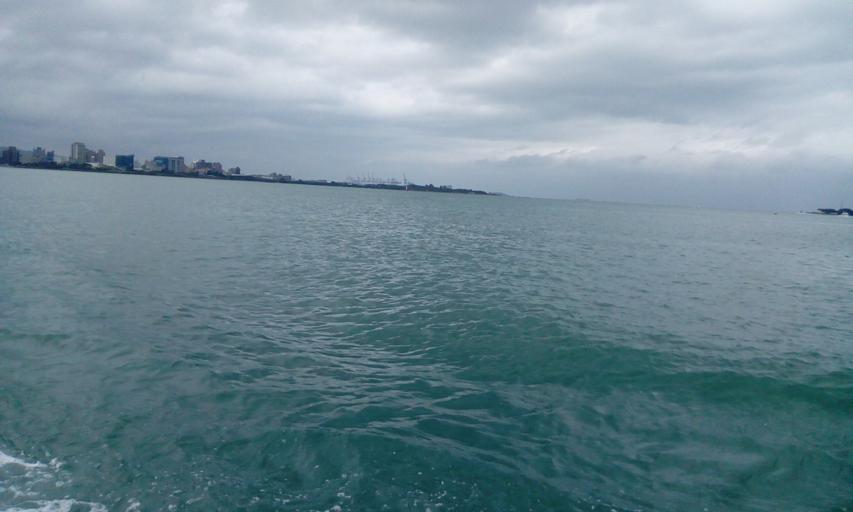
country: TW
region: Taipei
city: Taipei
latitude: 25.1686
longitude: 121.4385
